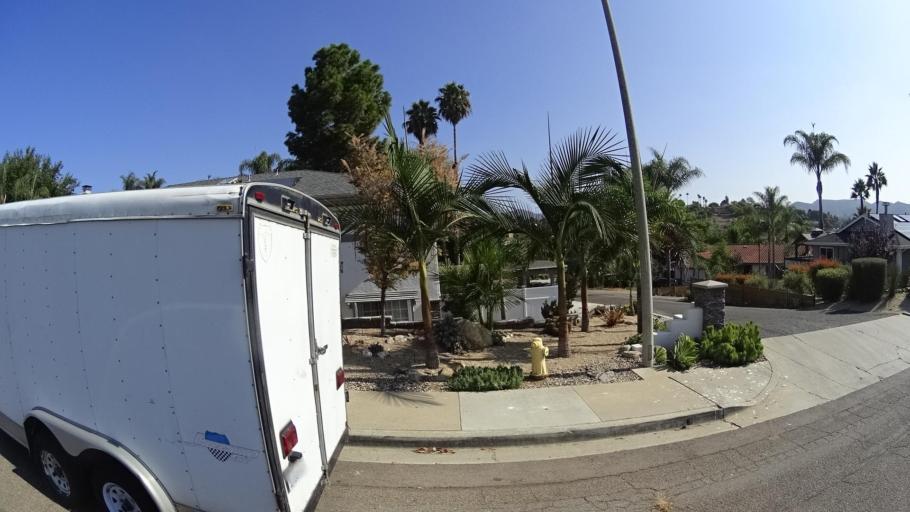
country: US
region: California
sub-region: San Diego County
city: Vista
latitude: 33.1782
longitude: -117.2193
